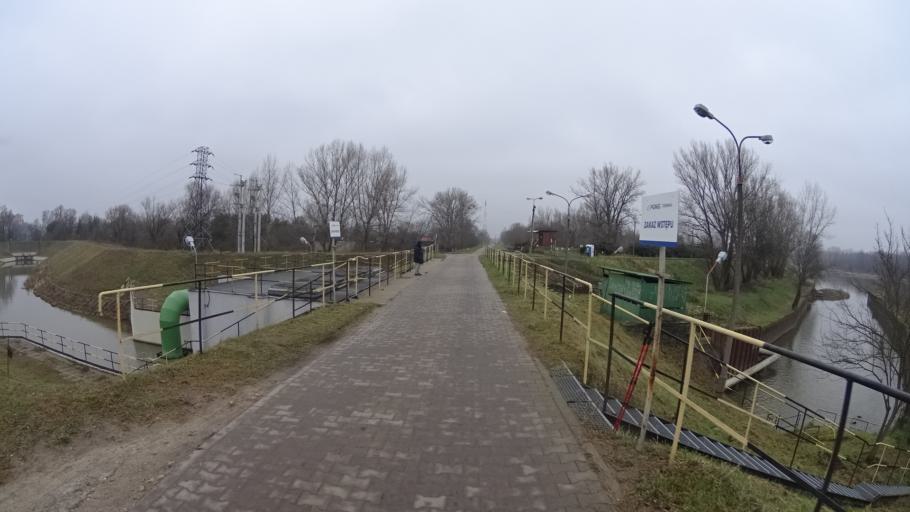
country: PL
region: Masovian Voivodeship
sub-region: Warszawa
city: Wilanow
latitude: 52.1904
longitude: 21.1028
